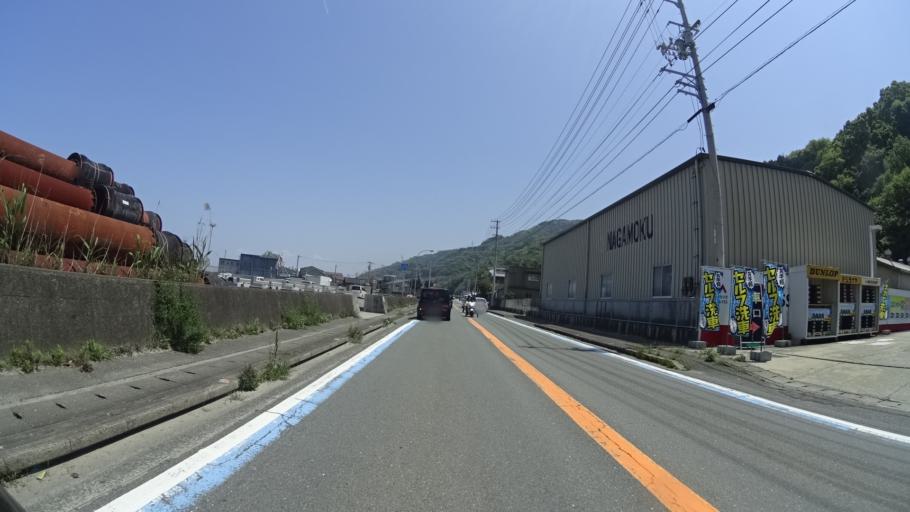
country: JP
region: Ehime
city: Ozu
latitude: 33.6168
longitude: 132.4894
